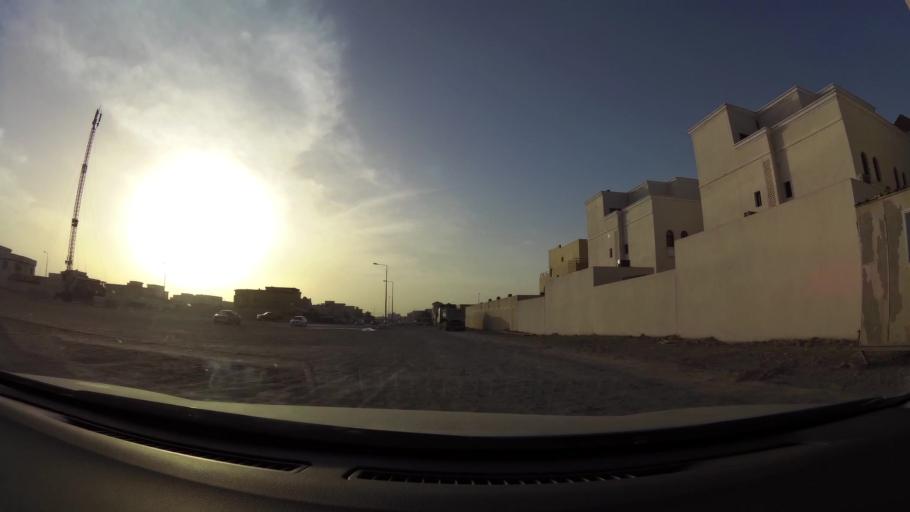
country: QA
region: Al Wakrah
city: Al Wakrah
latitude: 25.1489
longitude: 51.6070
